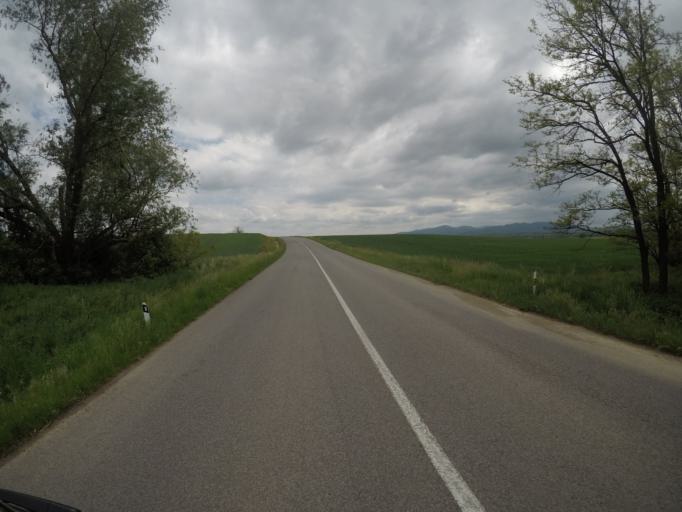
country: SK
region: Banskobystricky
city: Dudince
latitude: 48.0730
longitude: 18.8321
